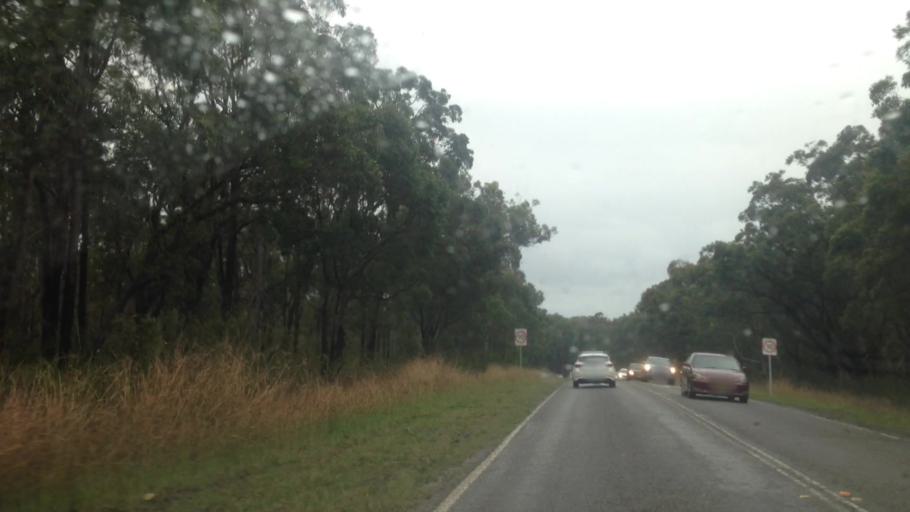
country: AU
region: New South Wales
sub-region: Lake Macquarie Shire
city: Dora Creek
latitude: -33.1497
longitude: 151.4792
